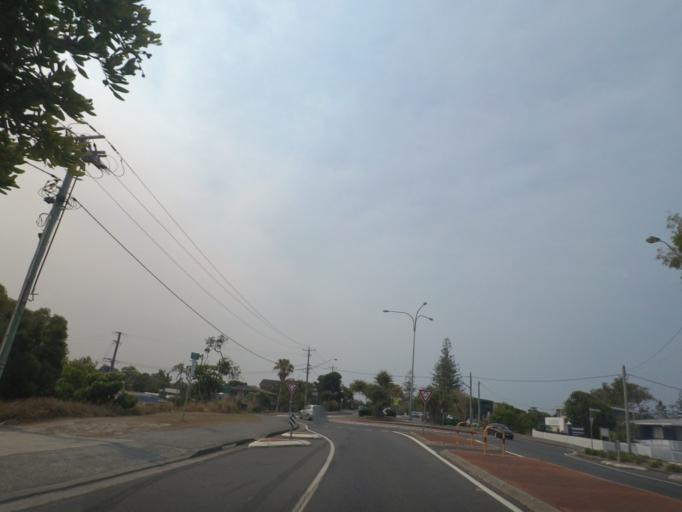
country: AU
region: New South Wales
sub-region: Tweed
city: Casuarina
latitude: -28.3310
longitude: 153.5692
